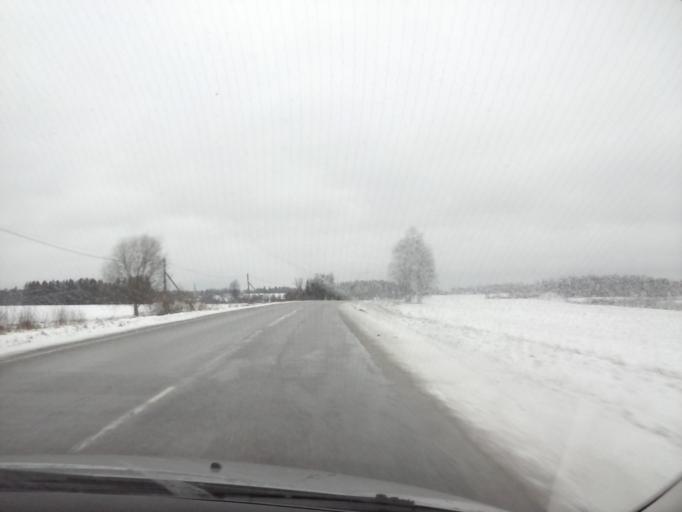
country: LV
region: Valkas Rajons
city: Valka
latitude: 57.7511
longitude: 25.9668
